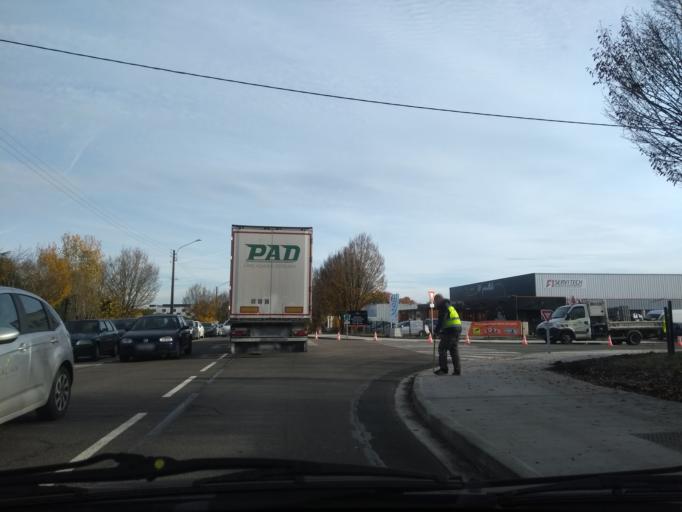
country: FR
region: Aquitaine
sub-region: Departement de la Gironde
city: Canejan
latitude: 44.7835
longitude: -0.6469
